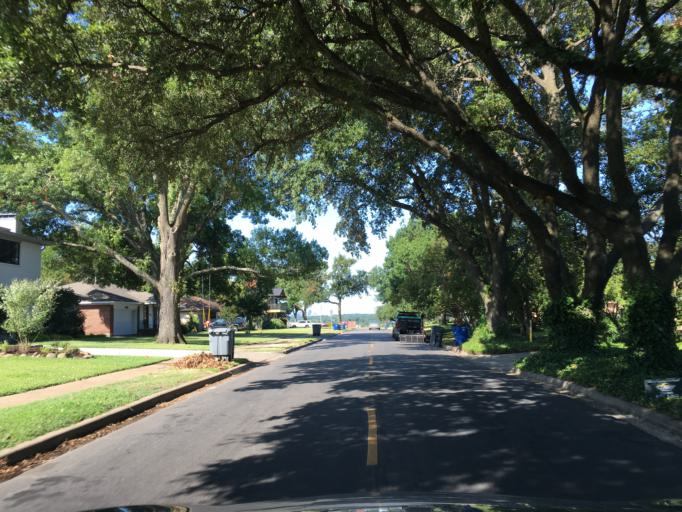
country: US
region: Texas
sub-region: Dallas County
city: Highland Park
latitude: 32.8544
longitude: -96.7144
